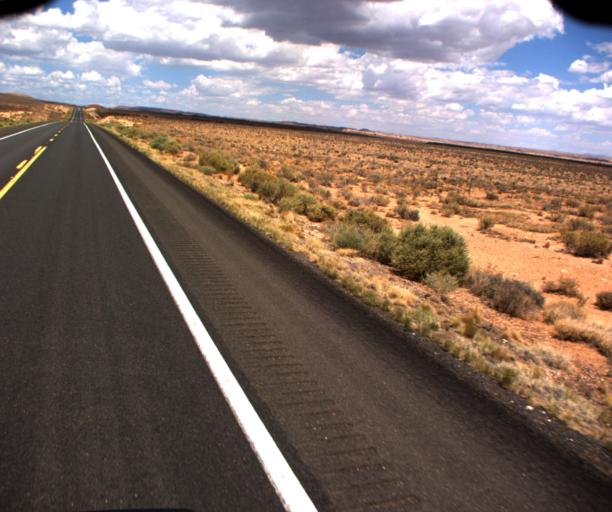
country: US
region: Arizona
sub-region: Coconino County
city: Tuba City
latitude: 35.8784
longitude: -111.5200
